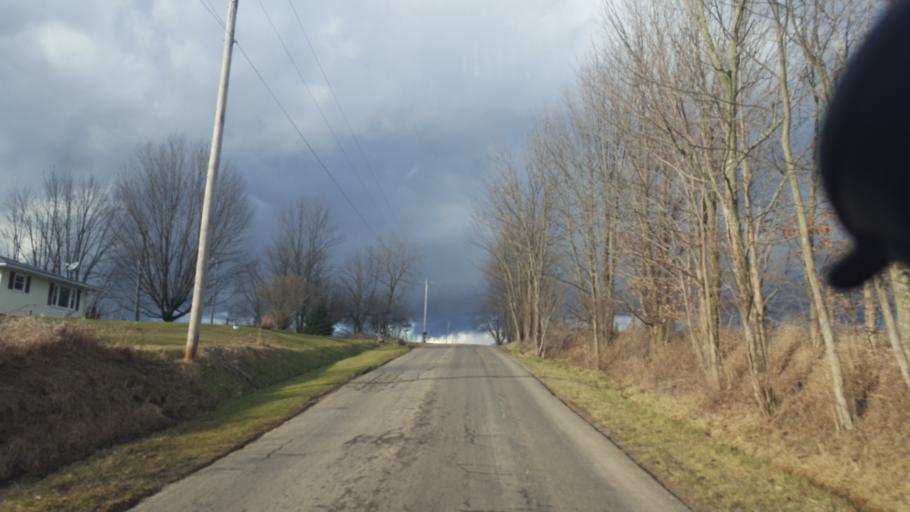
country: US
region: Ohio
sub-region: Knox County
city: Fredericktown
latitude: 40.5640
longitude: -82.6237
